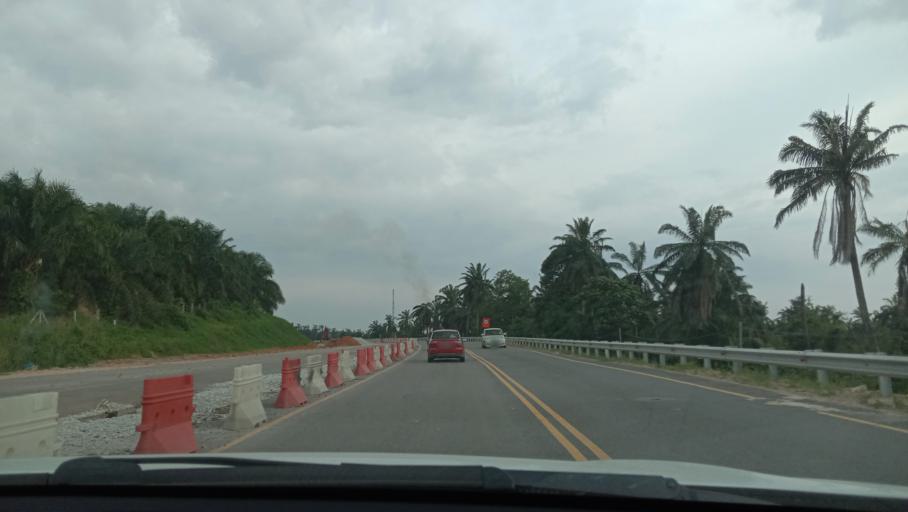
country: MY
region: Selangor
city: Batu Arang
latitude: 3.2702
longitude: 101.4542
